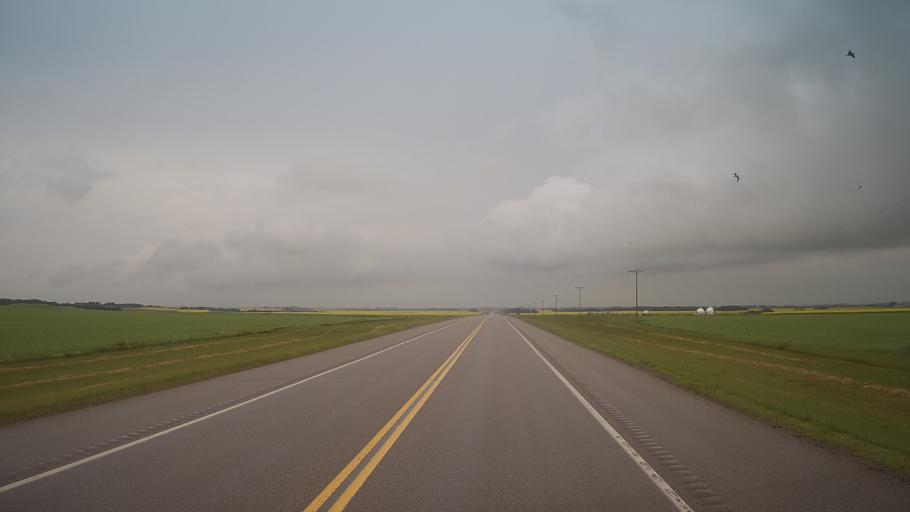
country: CA
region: Saskatchewan
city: Wilkie
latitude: 52.4181
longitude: -108.8895
